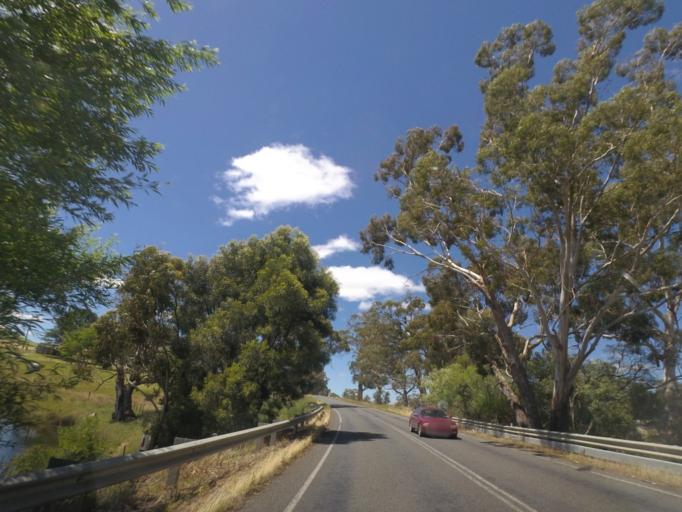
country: AU
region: Victoria
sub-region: Mount Alexander
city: Castlemaine
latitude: -37.3143
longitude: 144.2254
